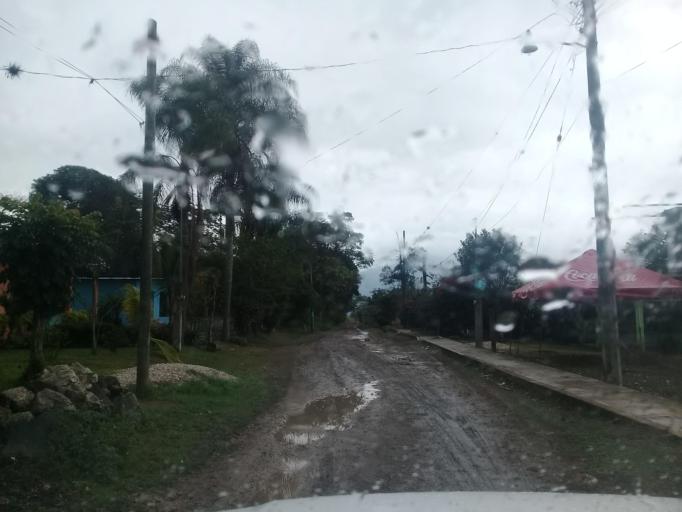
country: MX
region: Veracruz
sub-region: Amatlan de los Reyes
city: Trapiche Viejo
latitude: 18.8412
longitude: -96.9473
